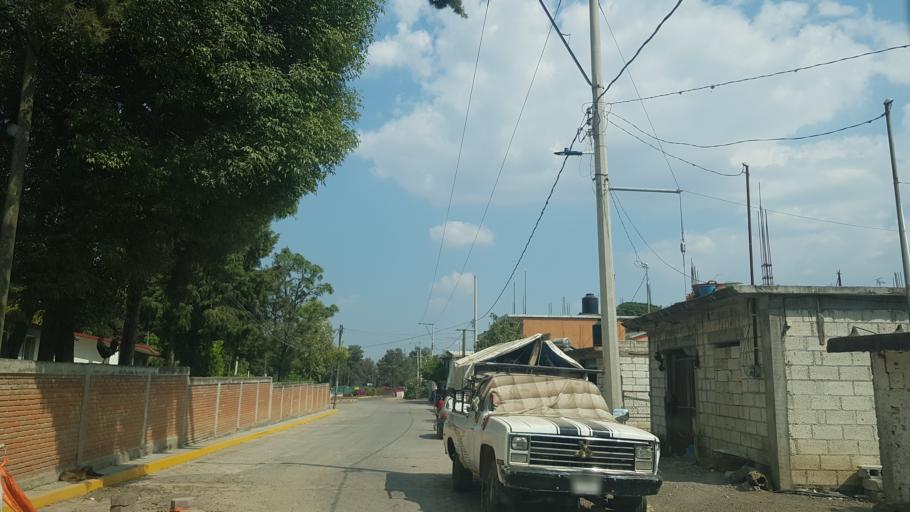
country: MX
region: Puebla
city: San Juan Amecac
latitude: 18.8317
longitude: -98.6603
